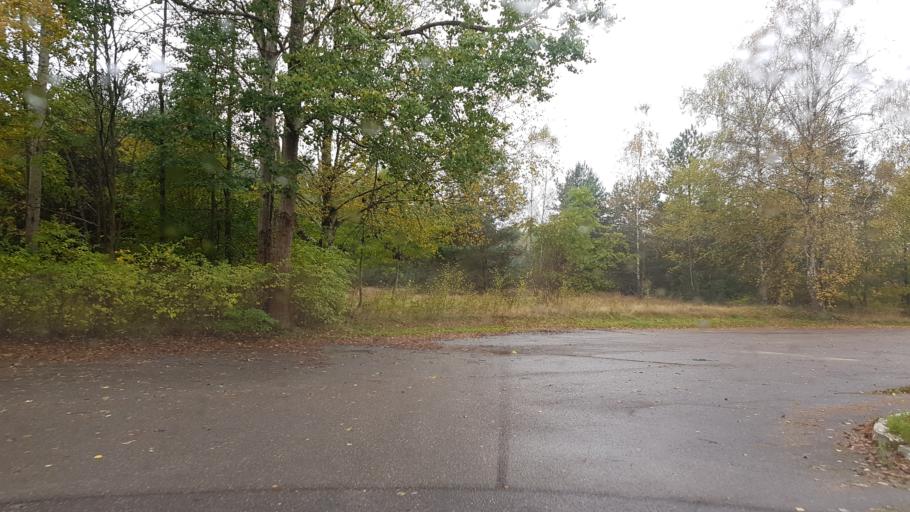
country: PL
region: West Pomeranian Voivodeship
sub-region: Powiat walecki
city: Walcz
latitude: 53.3837
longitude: 16.4874
